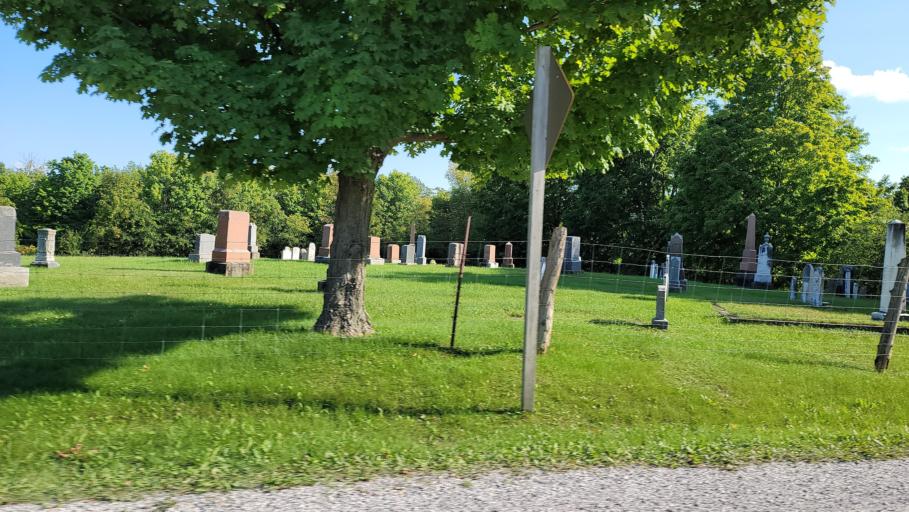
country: CA
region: Ontario
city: Perth
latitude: 45.0152
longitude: -76.2347
